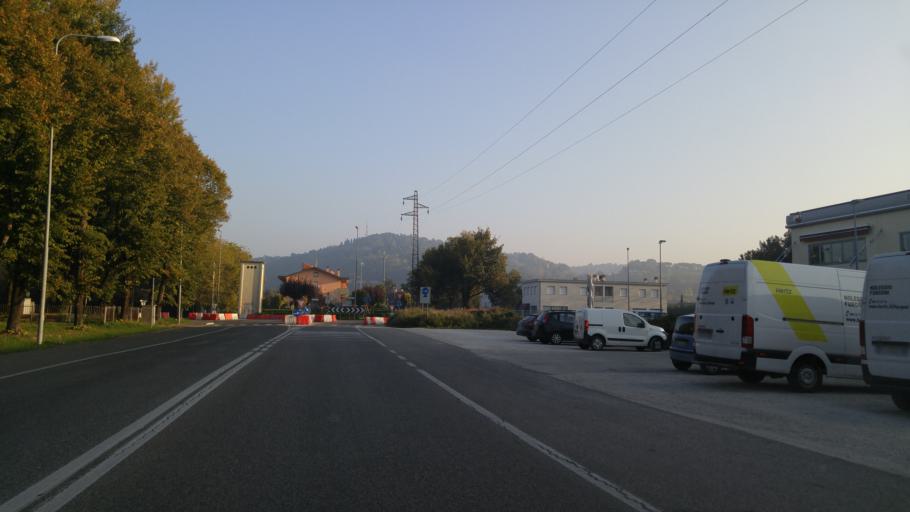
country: IT
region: The Marches
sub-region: Provincia di Pesaro e Urbino
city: Pesaro
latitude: 43.8948
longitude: 12.8856
